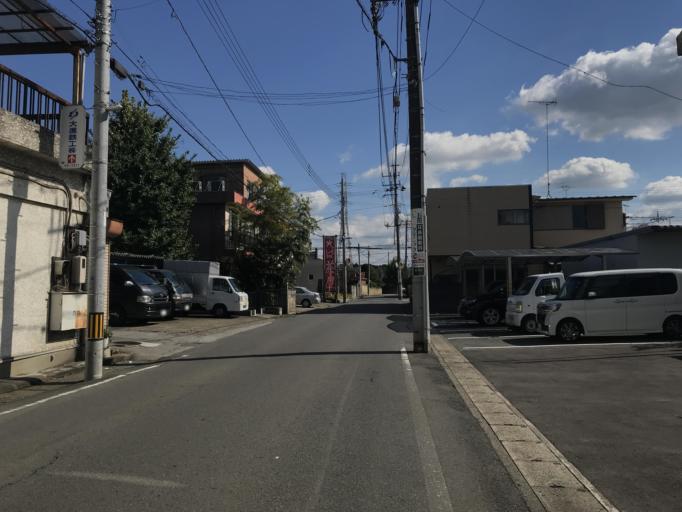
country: JP
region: Tochigi
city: Oyama
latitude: 36.2668
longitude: 139.7663
